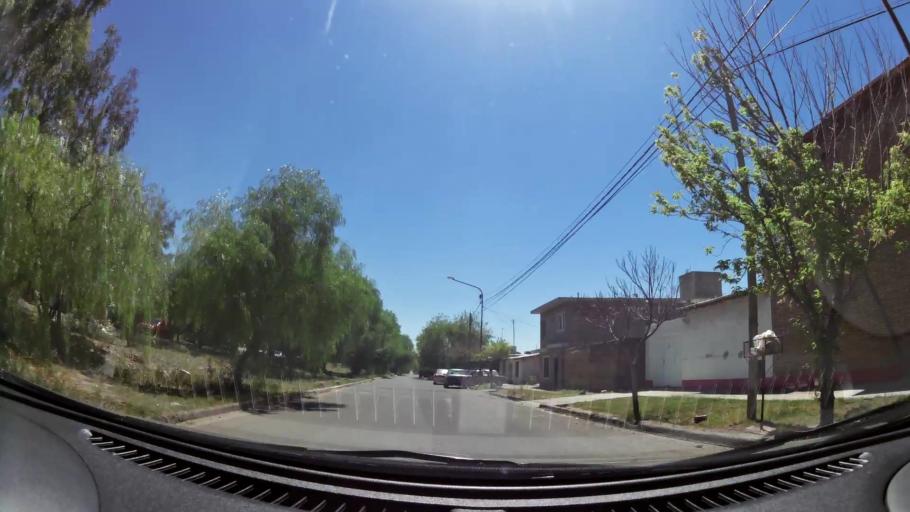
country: AR
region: Mendoza
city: Las Heras
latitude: -32.8439
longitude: -68.8732
